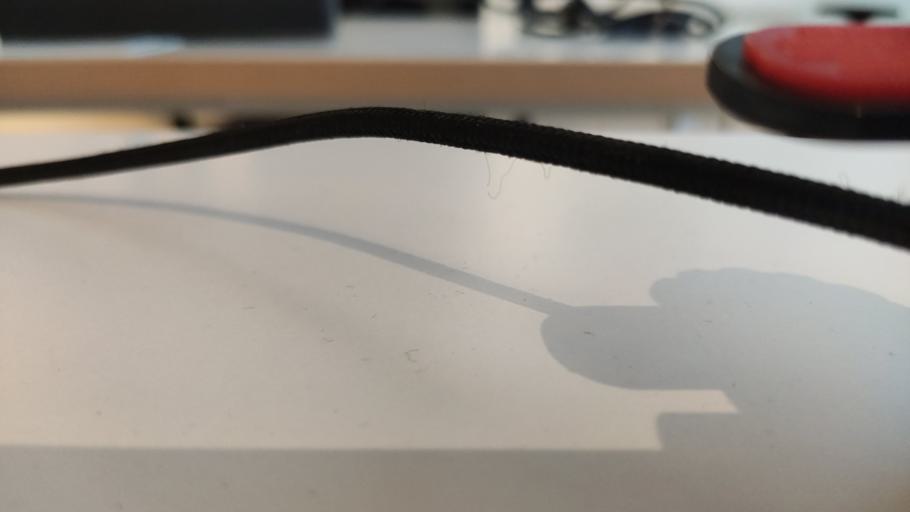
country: RU
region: Moskovskaya
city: Novopetrovskoye
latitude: 55.9402
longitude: 36.4356
